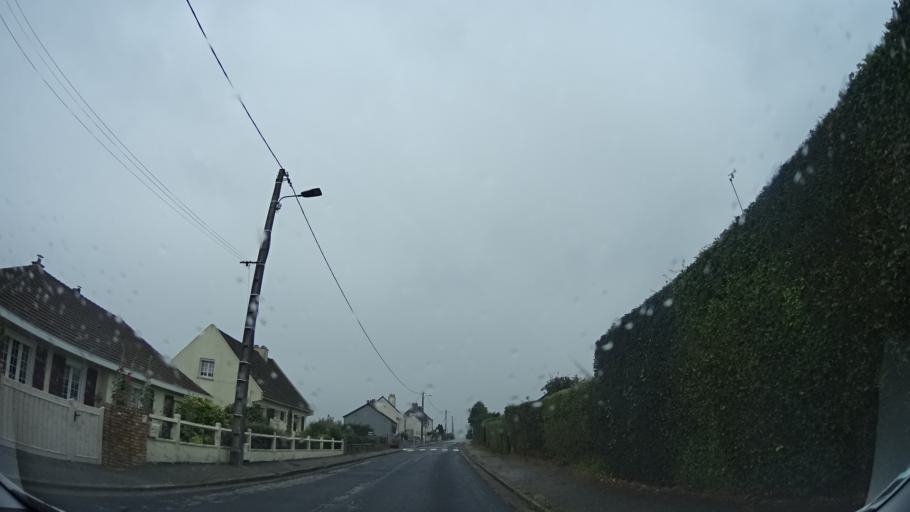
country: FR
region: Lower Normandy
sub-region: Departement de la Manche
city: Octeville
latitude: 49.6215
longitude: -1.6545
